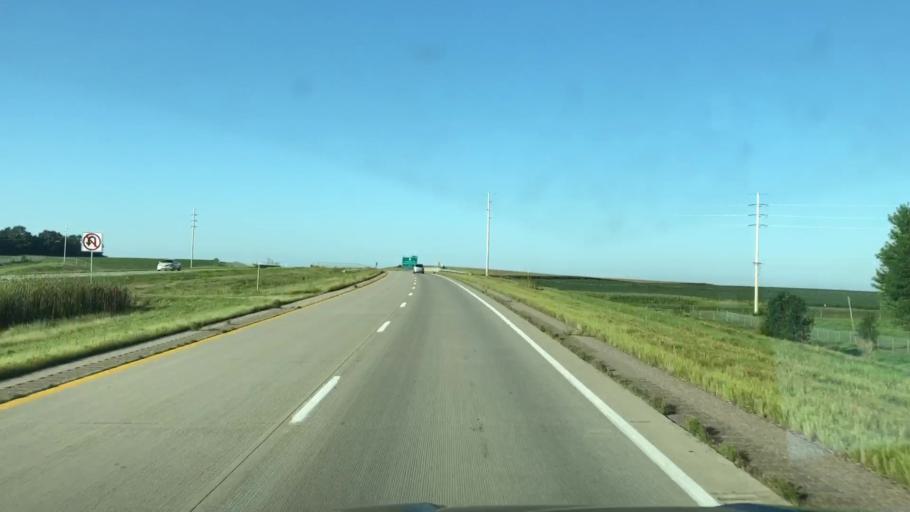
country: US
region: Iowa
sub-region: Plymouth County
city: Le Mars
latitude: 42.8136
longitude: -96.1922
